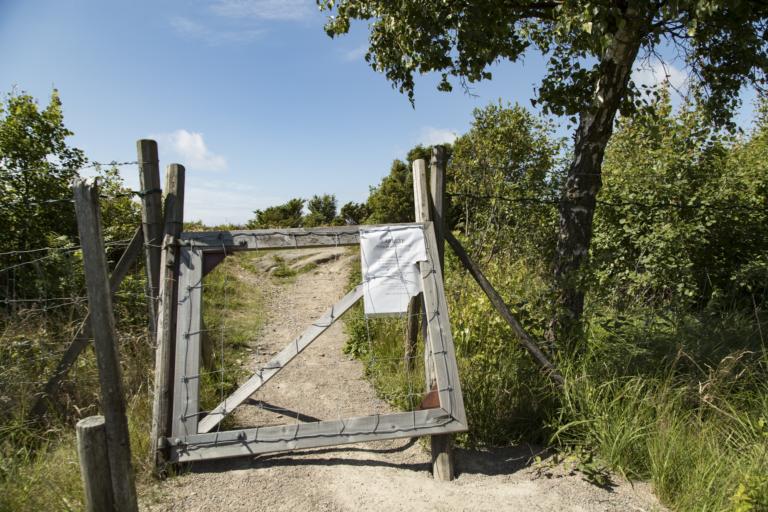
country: SE
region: Halland
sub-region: Varbergs Kommun
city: Varberg
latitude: 57.0943
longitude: 12.2455
